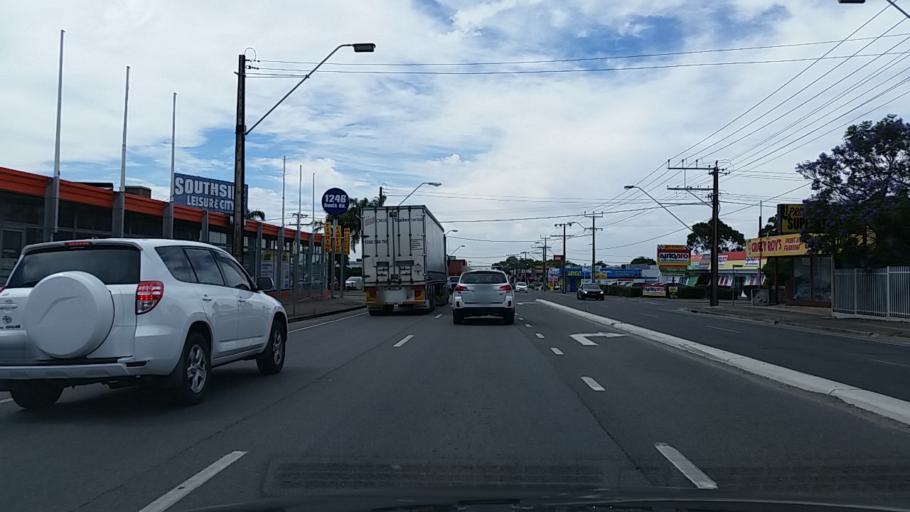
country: AU
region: South Australia
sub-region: Marion
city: Clovelly Park
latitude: -35.0026
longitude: 138.5756
